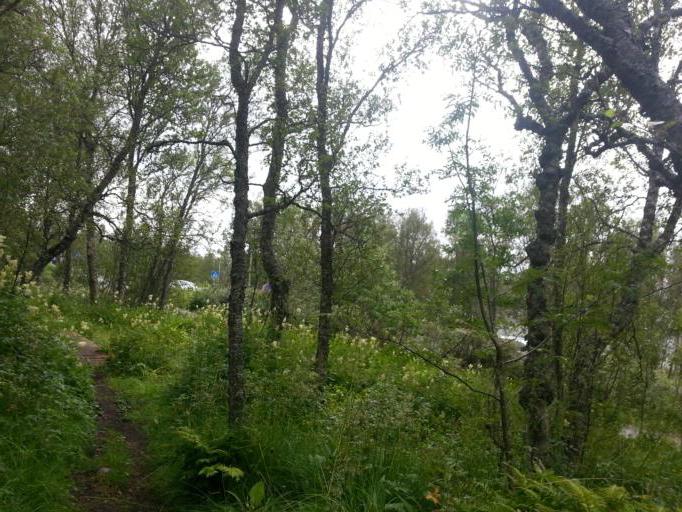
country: NO
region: Troms
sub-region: Tromso
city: Tromso
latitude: 69.6353
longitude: 18.9061
